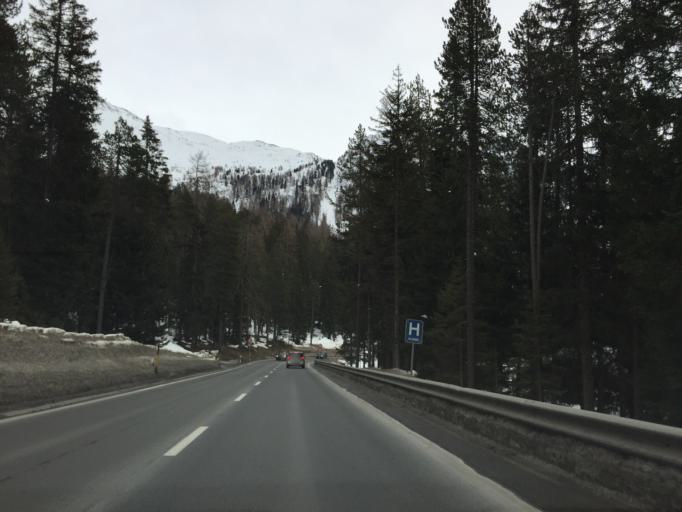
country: CH
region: Grisons
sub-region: Praettigau/Davos District
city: Davos
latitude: 46.8308
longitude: 9.8562
